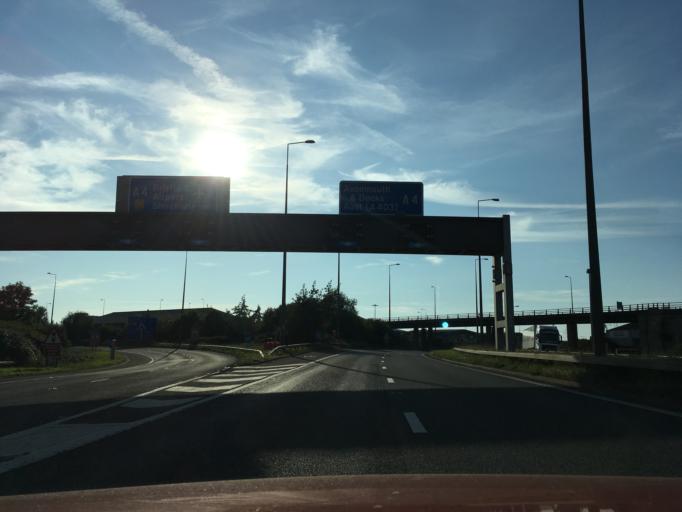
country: GB
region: England
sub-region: North Somerset
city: Easton-in-Gordano
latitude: 51.4999
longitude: -2.6874
